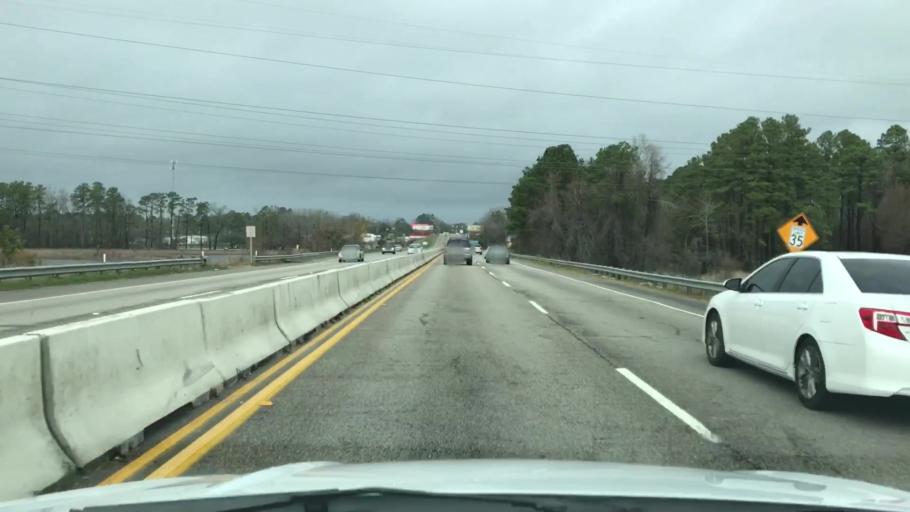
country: US
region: South Carolina
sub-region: Horry County
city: Conway
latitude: 33.8255
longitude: -79.0544
